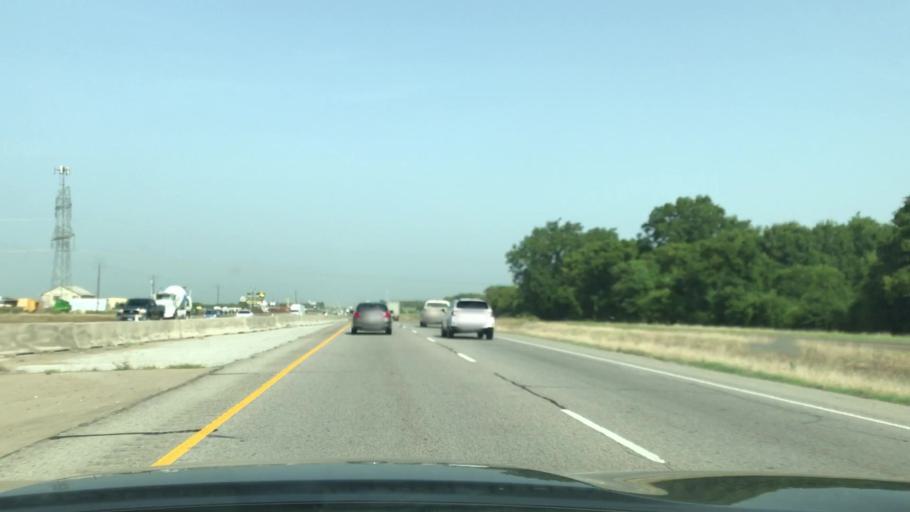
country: US
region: Texas
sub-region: Kaufman County
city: Forney
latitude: 32.7764
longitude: -96.5125
